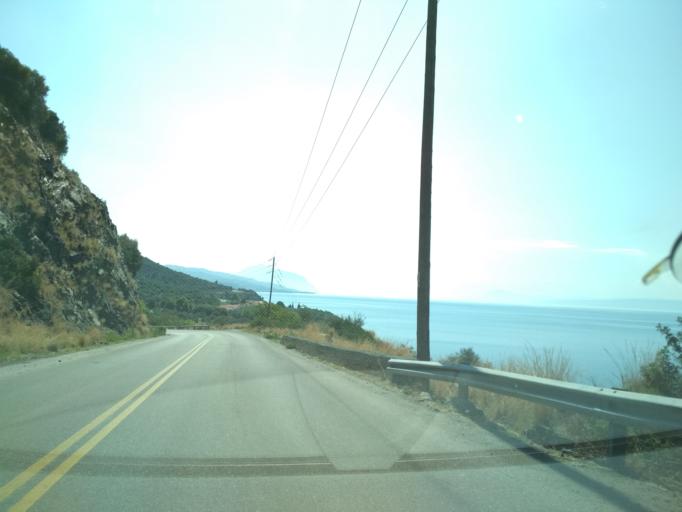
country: GR
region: Central Greece
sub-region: Nomos Evvoias
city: Roviai
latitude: 38.8447
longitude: 23.1653
